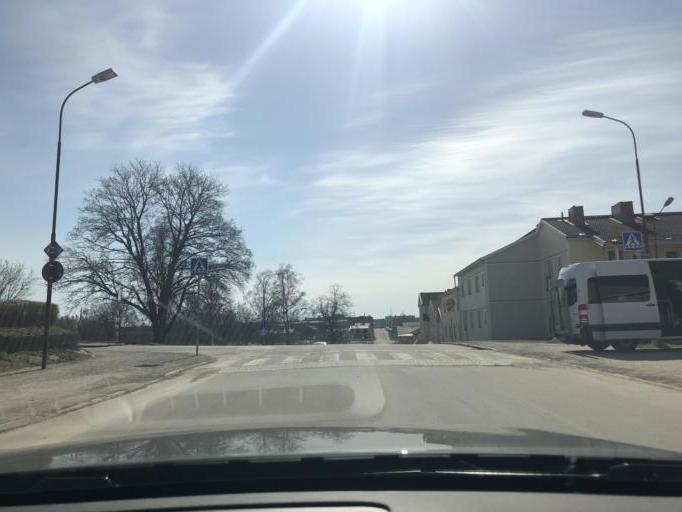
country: SE
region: Gaevleborg
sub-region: Hudiksvalls Kommun
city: Hudiksvall
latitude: 61.7283
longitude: 17.1223
